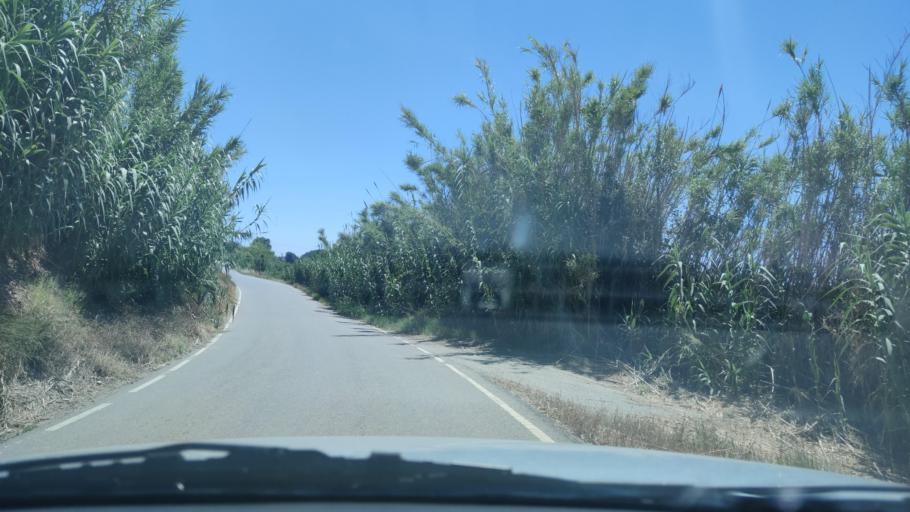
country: ES
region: Catalonia
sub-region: Provincia de Lleida
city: Alcoletge
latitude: 41.6361
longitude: 0.6565
